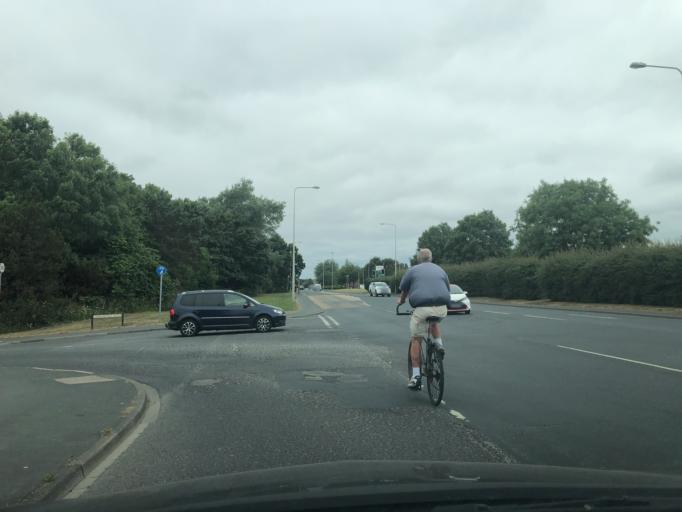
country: GB
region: England
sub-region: North Yorkshire
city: Scarborough
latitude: 54.2392
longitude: -0.4074
